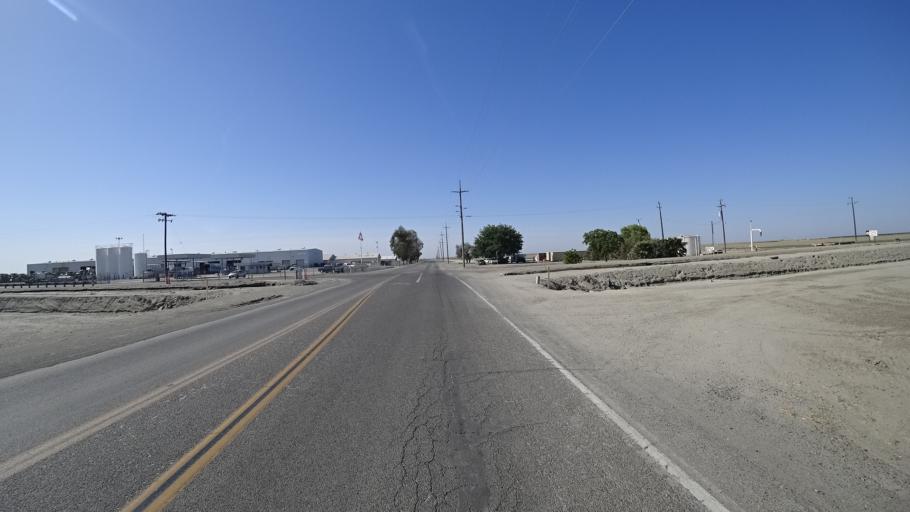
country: US
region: California
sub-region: Kings County
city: Corcoran
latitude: 36.0657
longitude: -119.5720
